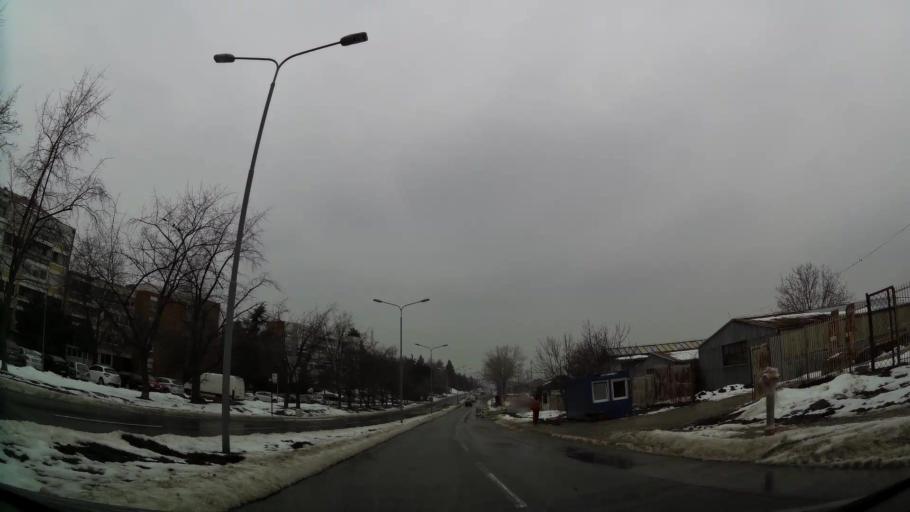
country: RS
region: Central Serbia
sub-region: Belgrade
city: Zvezdara
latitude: 44.7517
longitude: 20.5031
